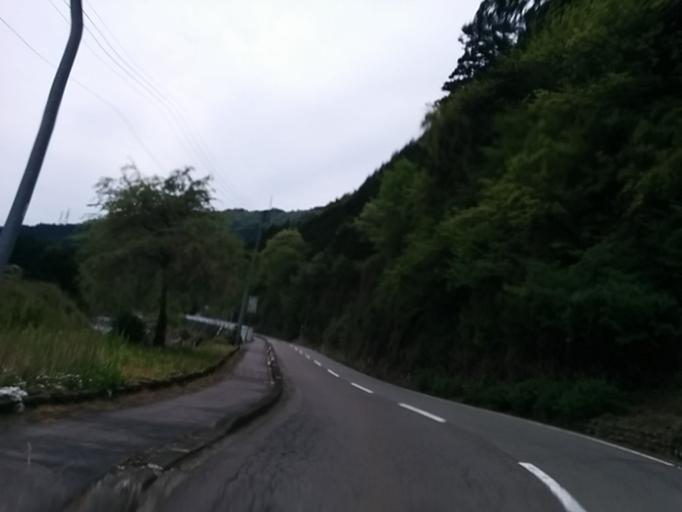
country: JP
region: Gifu
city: Gujo
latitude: 35.7461
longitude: 137.1049
